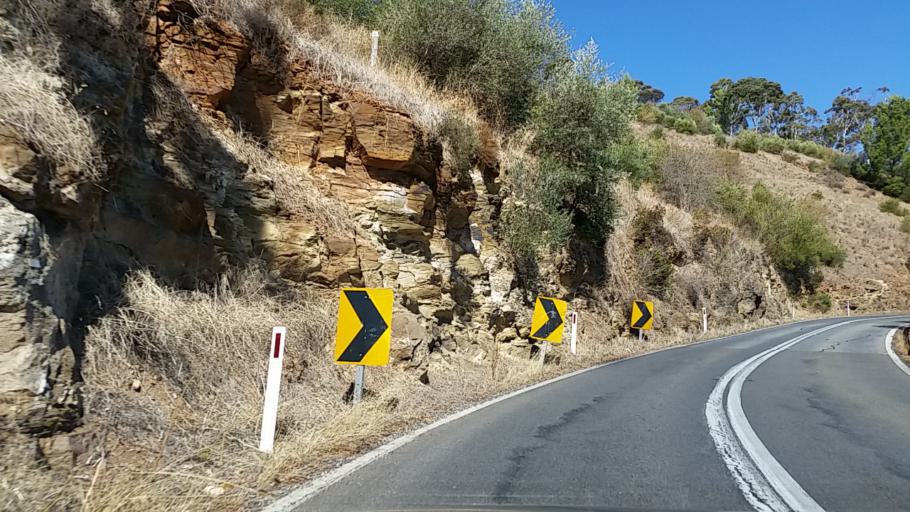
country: AU
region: South Australia
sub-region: Burnside
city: Beaumont
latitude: -34.9468
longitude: 138.6722
